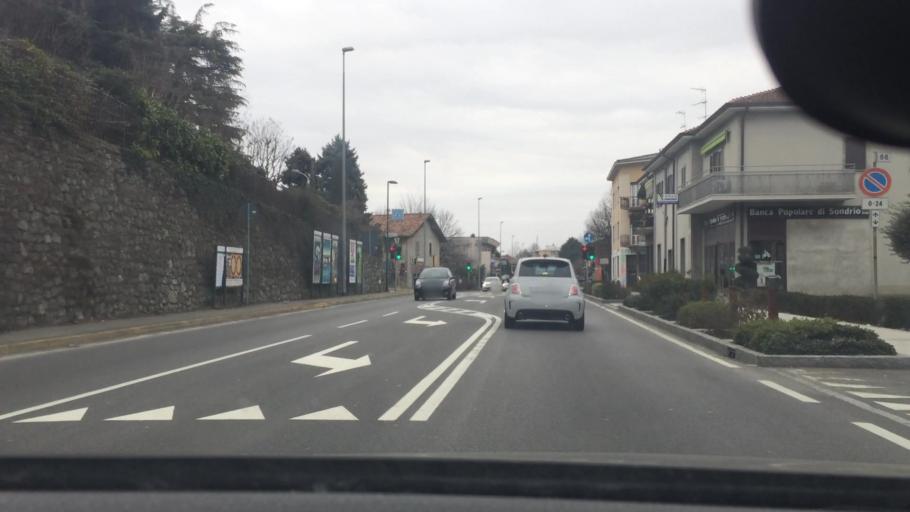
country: IT
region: Lombardy
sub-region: Provincia di Como
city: Lurago d'Erba
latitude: 45.7526
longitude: 9.2225
